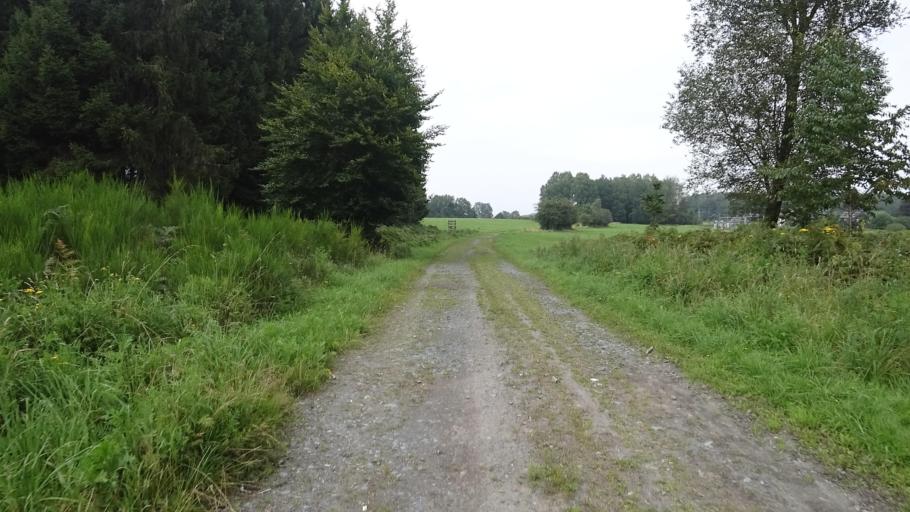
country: BE
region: Wallonia
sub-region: Province du Luxembourg
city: Chiny
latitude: 49.7937
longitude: 5.3282
